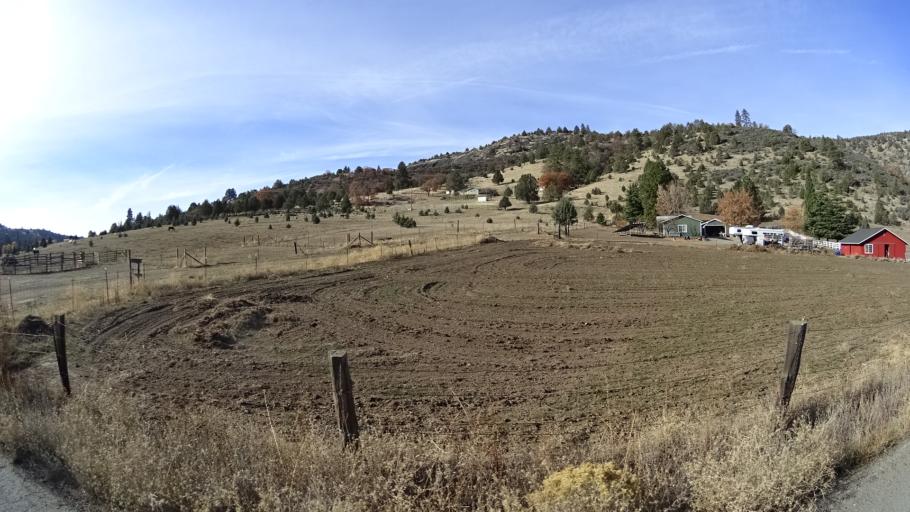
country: US
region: California
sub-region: Siskiyou County
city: Montague
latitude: 41.5971
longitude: -122.5766
